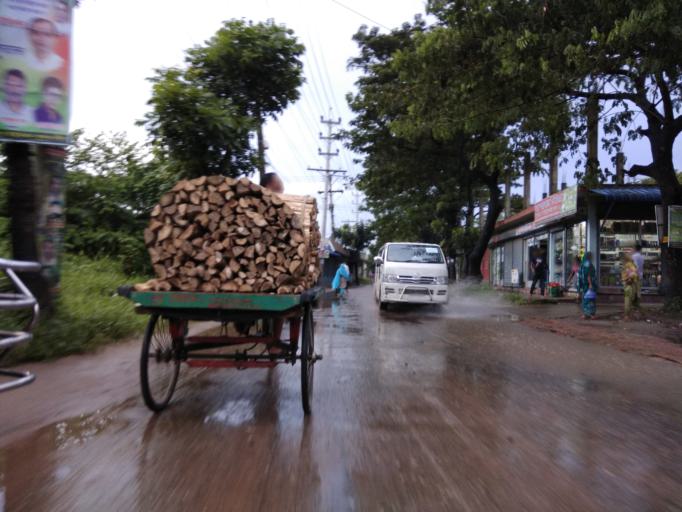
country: BD
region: Dhaka
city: Azimpur
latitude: 23.6661
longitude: 90.3055
